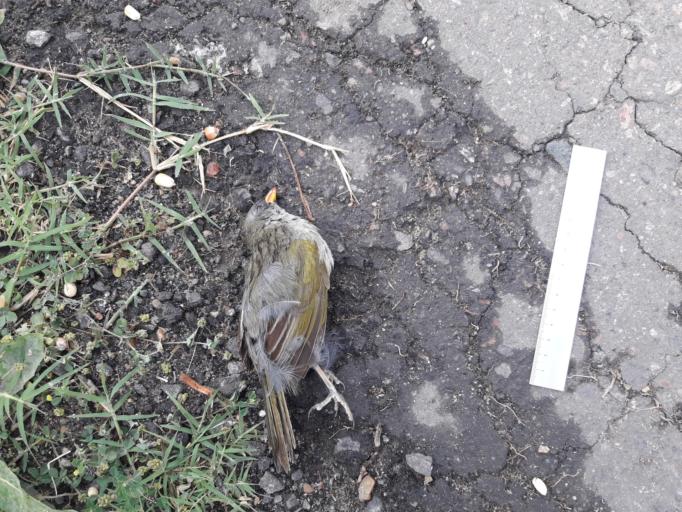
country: AR
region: Santa Fe
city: Santa Fe de la Vera Cruz
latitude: -31.6539
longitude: -60.6122
